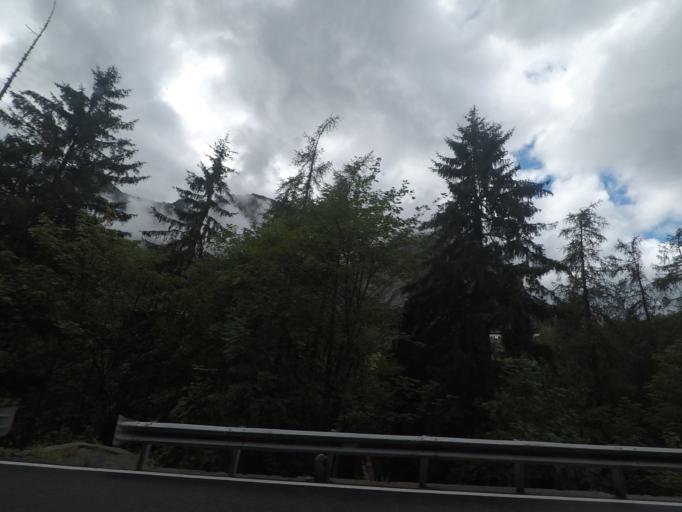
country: IT
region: Aosta Valley
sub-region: Valle d'Aosta
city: Valtournenche
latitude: 45.8710
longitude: 7.6231
